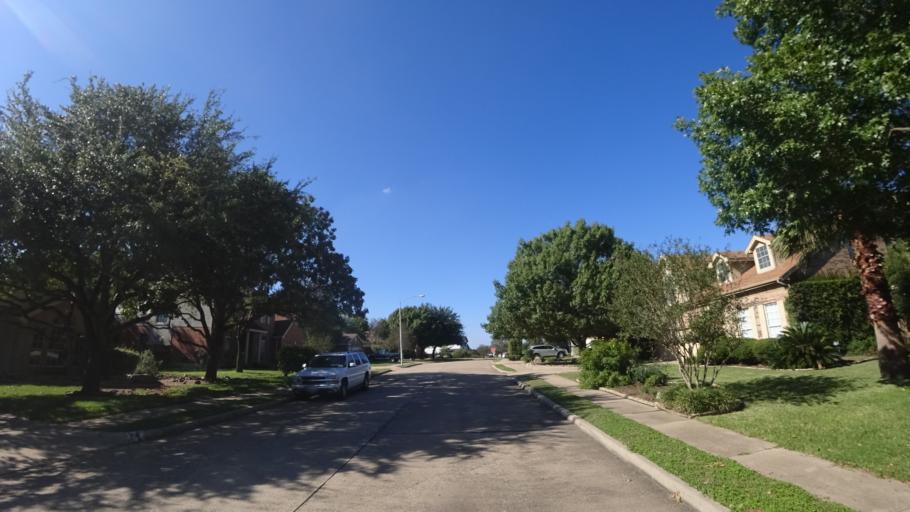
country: US
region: Texas
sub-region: Travis County
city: Manor
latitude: 30.3543
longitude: -97.6133
